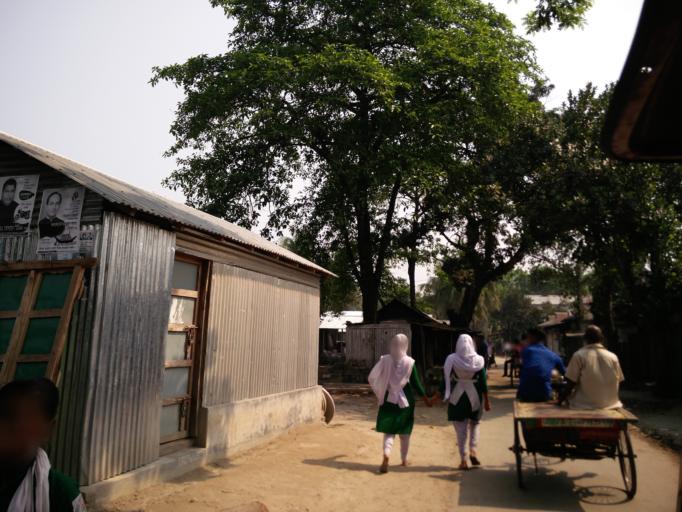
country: BD
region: Dhaka
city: Muktagacha
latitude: 24.9164
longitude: 90.2321
